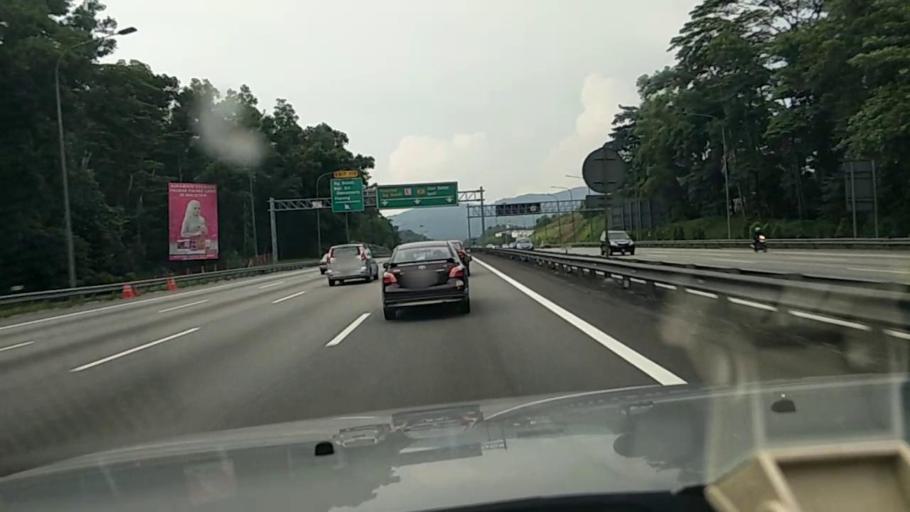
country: MY
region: Selangor
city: Kampung Baru Subang
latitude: 3.1956
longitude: 101.5825
